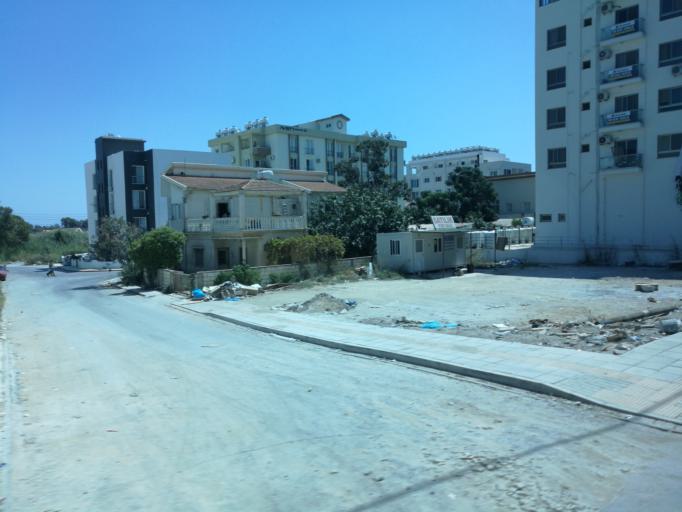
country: CY
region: Ammochostos
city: Famagusta
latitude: 35.1390
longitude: 33.9172
